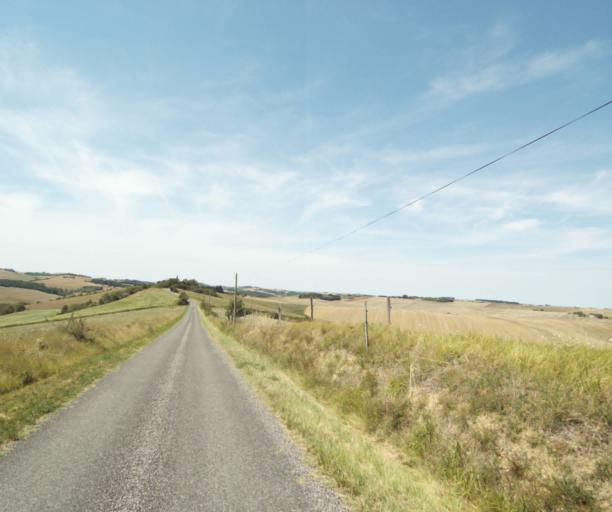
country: FR
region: Midi-Pyrenees
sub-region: Departement de l'Ariege
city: Lezat-sur-Leze
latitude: 43.2515
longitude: 1.3262
